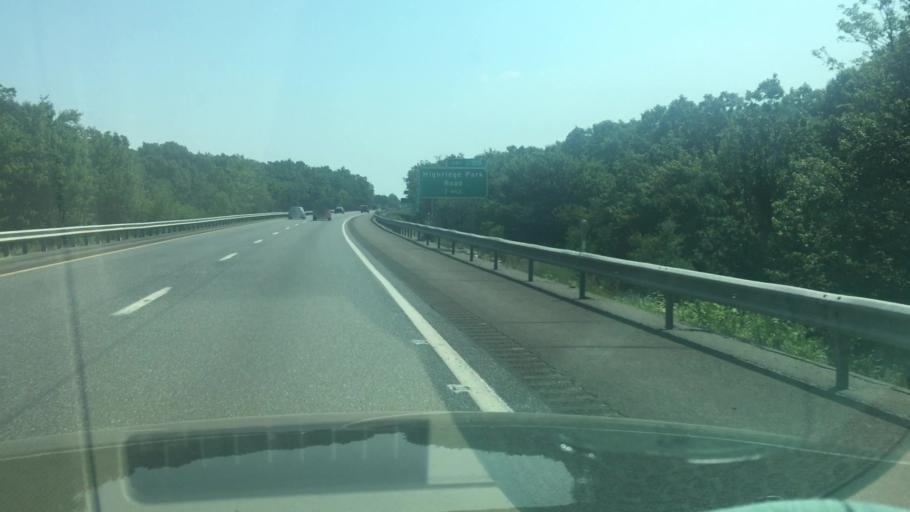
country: US
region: Pennsylvania
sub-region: Schuylkill County
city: Ashland
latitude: 40.7257
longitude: -76.3275
